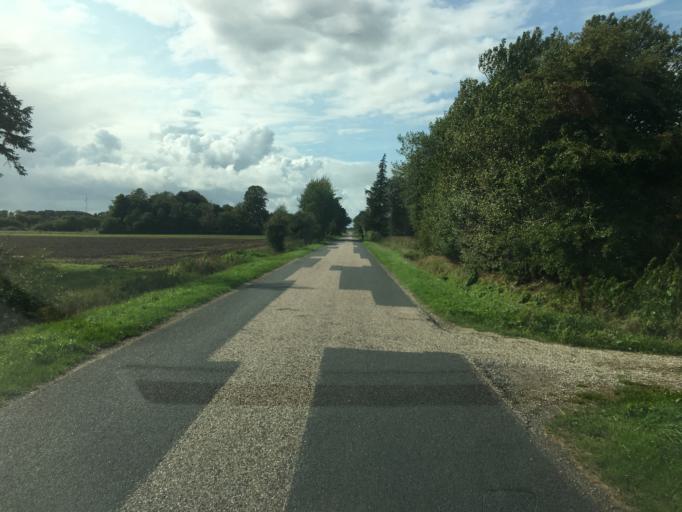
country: DK
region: South Denmark
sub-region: Tonder Kommune
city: Tonder
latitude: 54.9791
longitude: 8.8367
